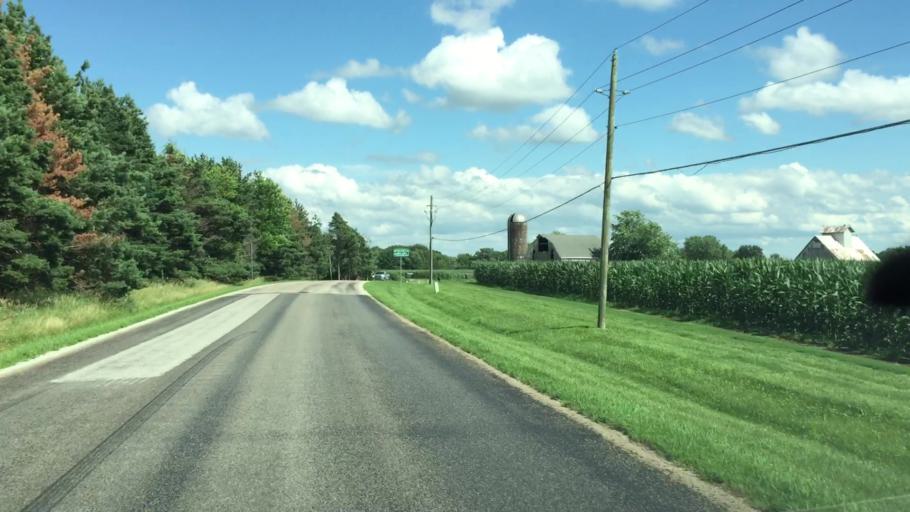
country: US
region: Iowa
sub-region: Linn County
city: Ely
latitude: 41.8160
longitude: -91.6182
